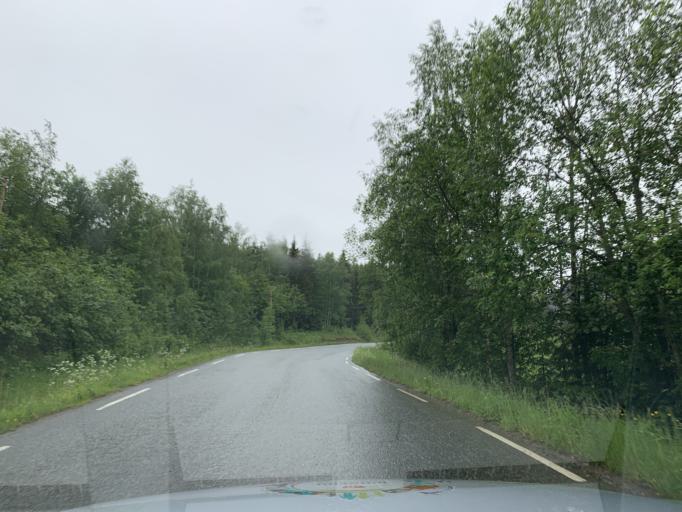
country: NO
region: Oppland
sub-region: Ringebu
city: Ringebu
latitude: 61.4455
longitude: 10.1700
